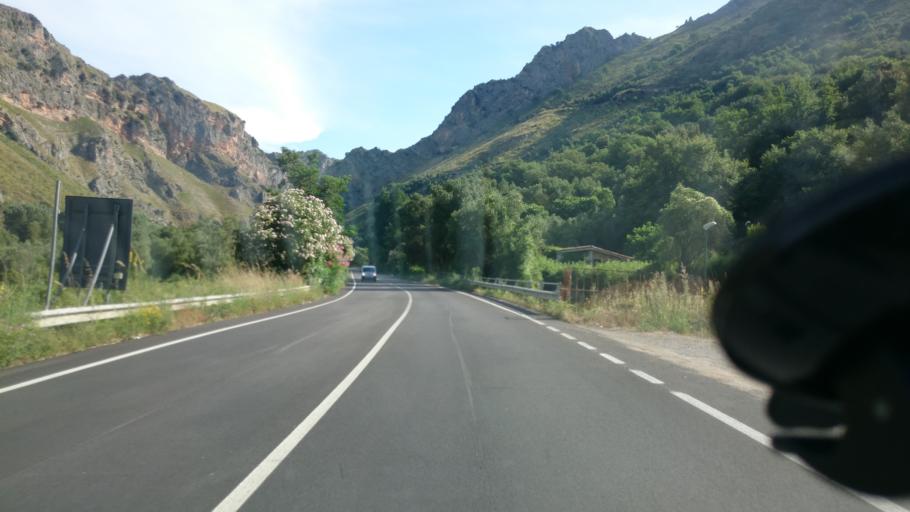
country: IT
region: Campania
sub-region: Provincia di Salerno
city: Centola
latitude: 40.0707
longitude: 15.3399
